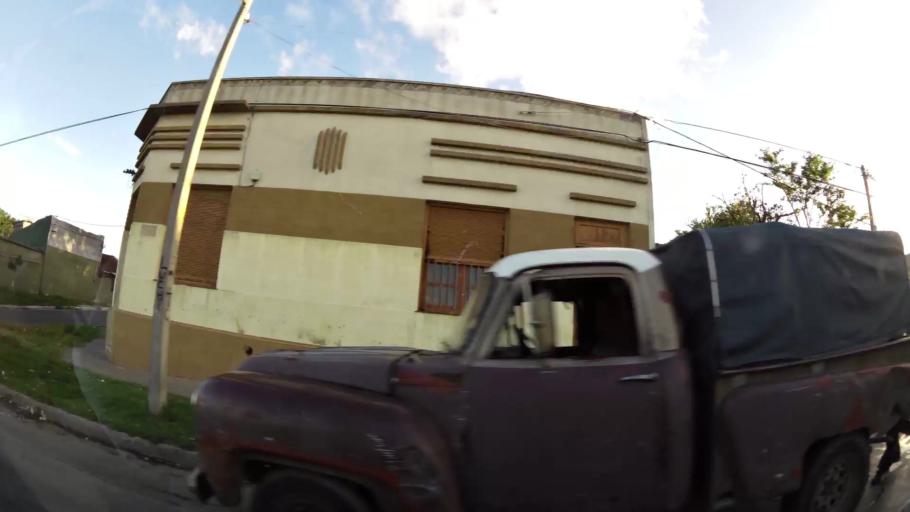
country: UY
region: Montevideo
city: Montevideo
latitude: -34.8841
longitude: -56.2573
